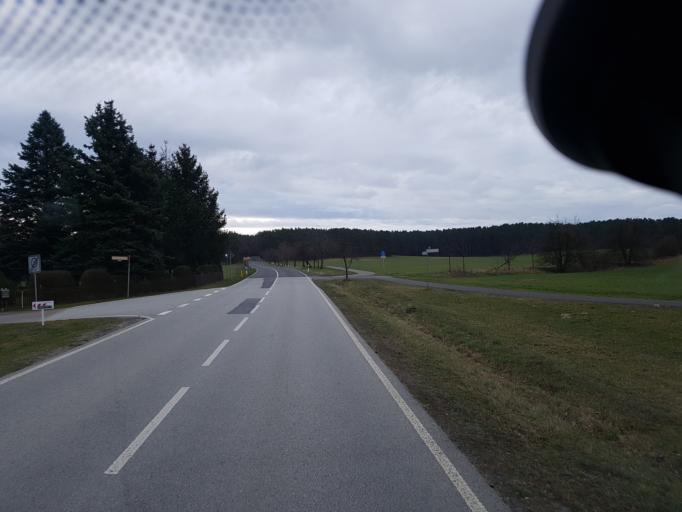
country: DE
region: Brandenburg
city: Mixdorf
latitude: 52.1889
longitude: 14.4668
